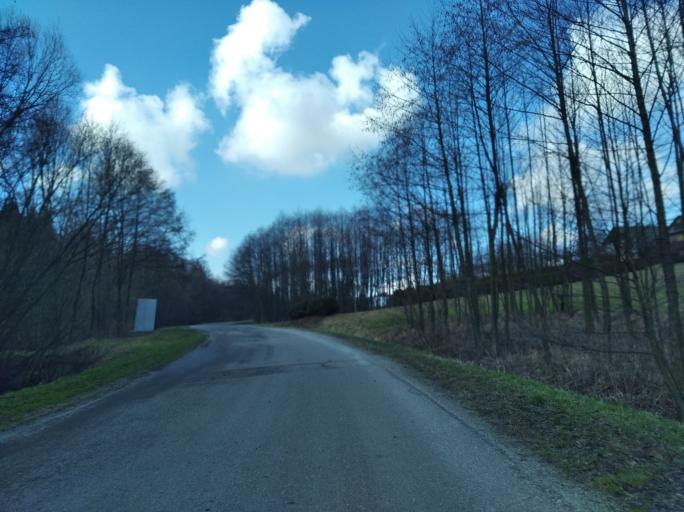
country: PL
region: Subcarpathian Voivodeship
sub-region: Powiat strzyzowski
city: Frysztak
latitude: 49.8694
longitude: 21.5347
